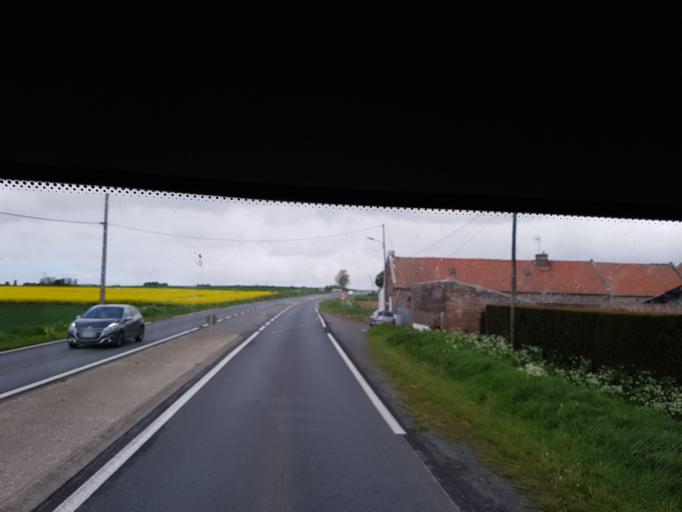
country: FR
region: Nord-Pas-de-Calais
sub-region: Departement du Nord
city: Raillencourt-Sainte-Olle
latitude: 50.2140
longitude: 3.1838
